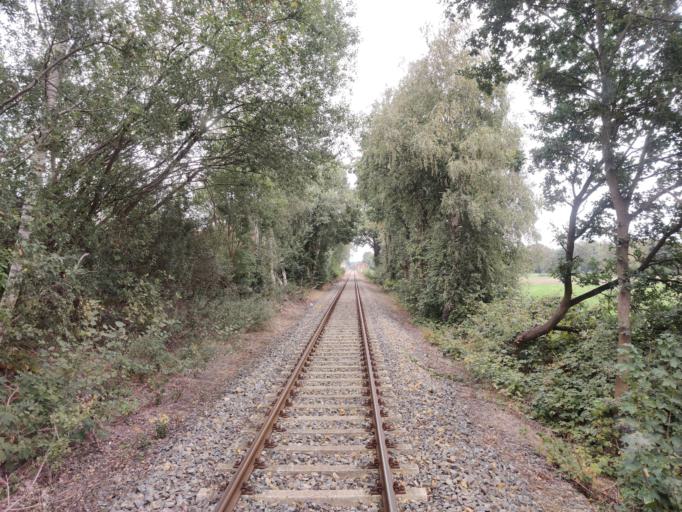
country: DE
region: Lower Saxony
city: Gnarrenburg
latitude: 53.3745
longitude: 9.0092
